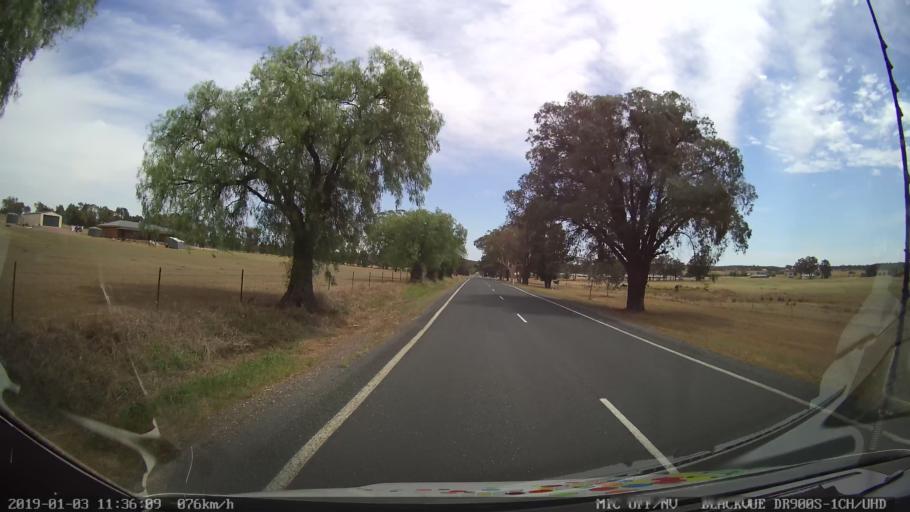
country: AU
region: New South Wales
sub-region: Weddin
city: Grenfell
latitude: -33.9140
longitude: 148.1595
